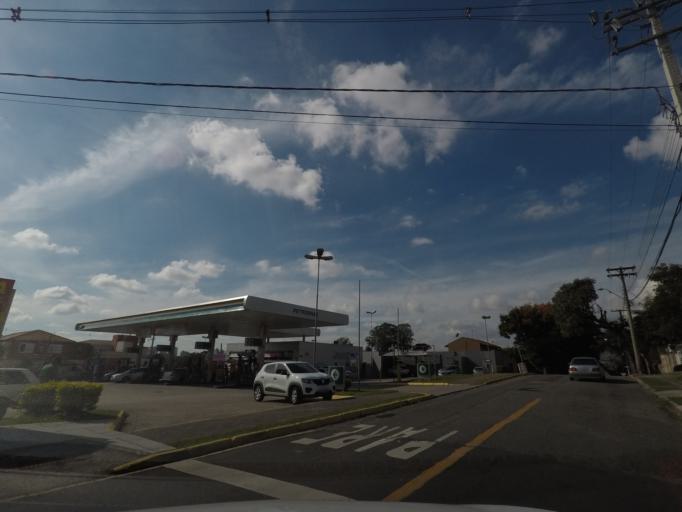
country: BR
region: Parana
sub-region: Pinhais
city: Pinhais
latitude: -25.4608
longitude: -49.2373
